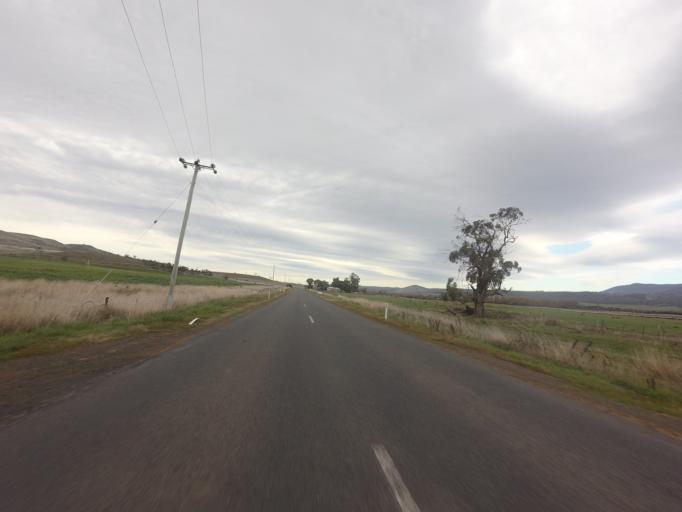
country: AU
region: Tasmania
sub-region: Derwent Valley
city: New Norfolk
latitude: -42.5001
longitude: 146.7330
